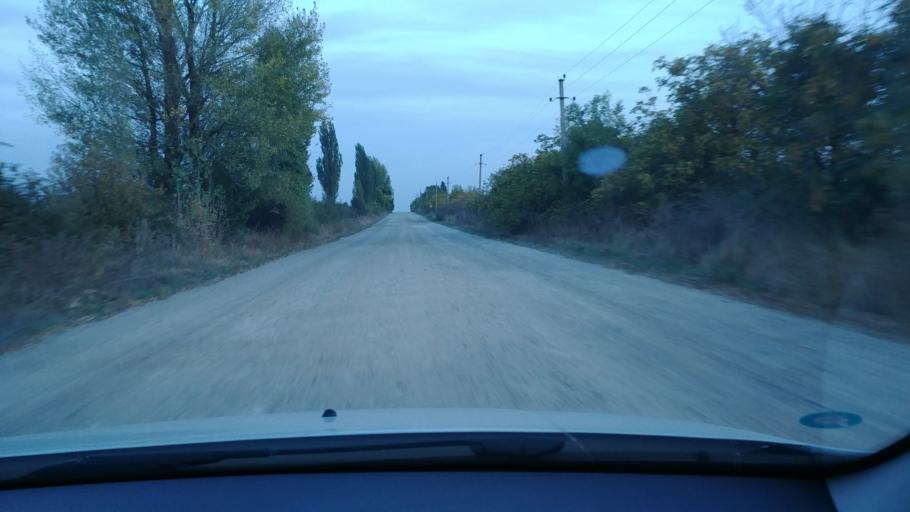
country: MD
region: Rezina
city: Saharna
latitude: 47.6716
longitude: 28.9398
